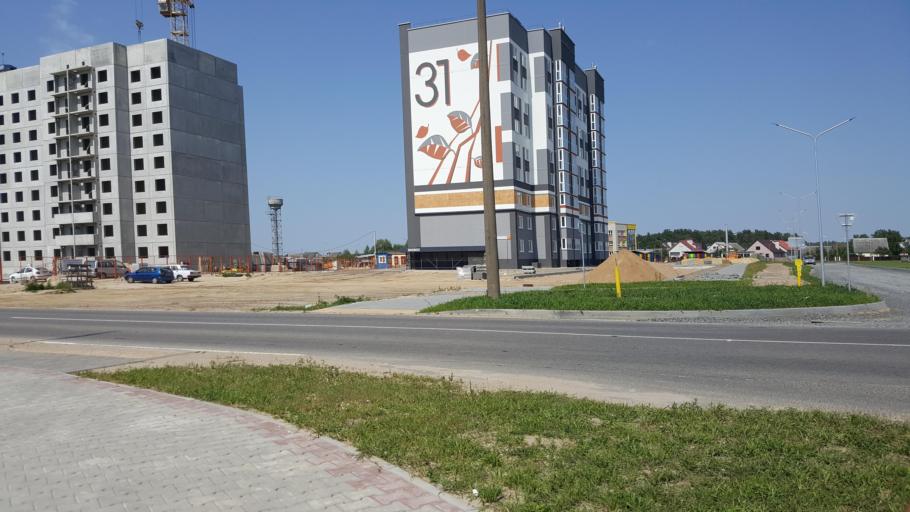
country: BY
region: Brest
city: Zhabinka
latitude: 52.1959
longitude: 24.0342
